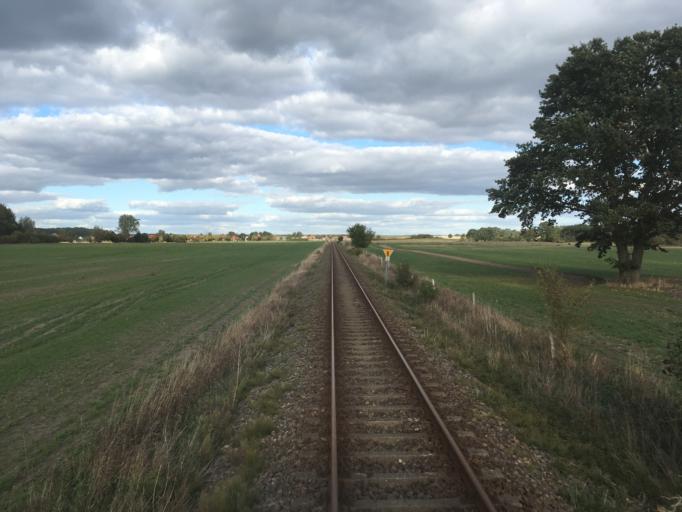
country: DE
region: Mecklenburg-Vorpommern
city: Malchow
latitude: 53.5118
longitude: 12.4323
